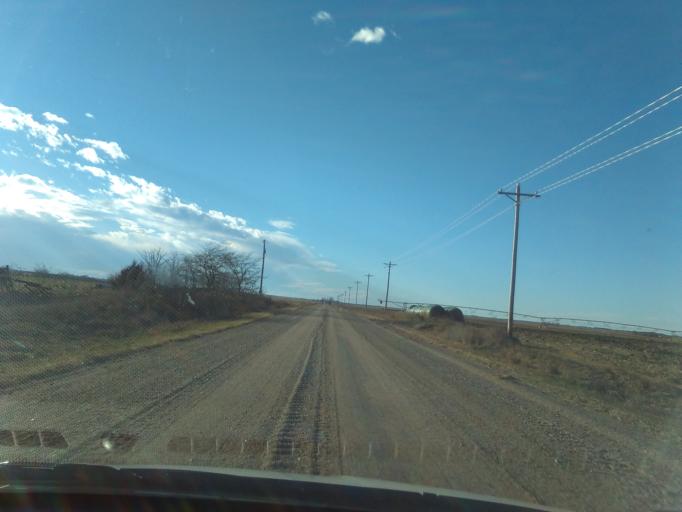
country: US
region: Nebraska
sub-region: Kearney County
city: Minden
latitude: 40.3649
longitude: -98.9816
